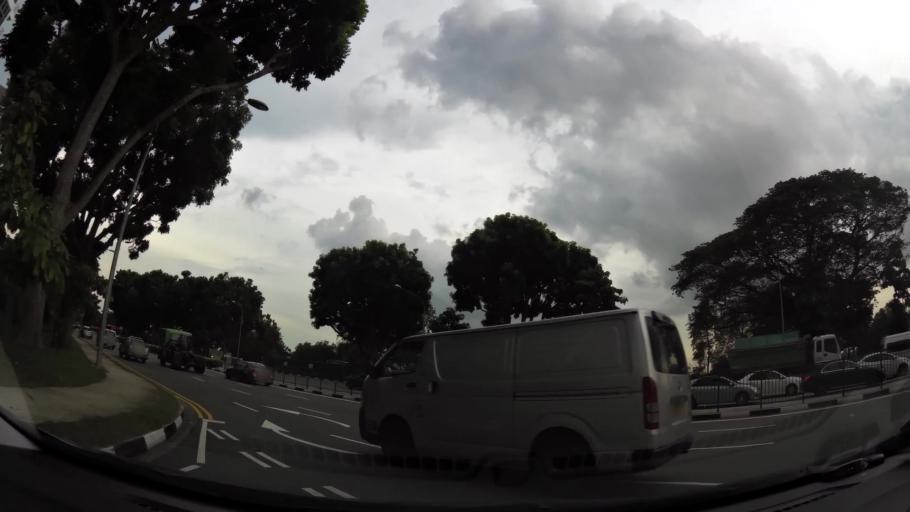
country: MY
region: Johor
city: Kampung Pasir Gudang Baru
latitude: 1.4101
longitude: 103.8301
